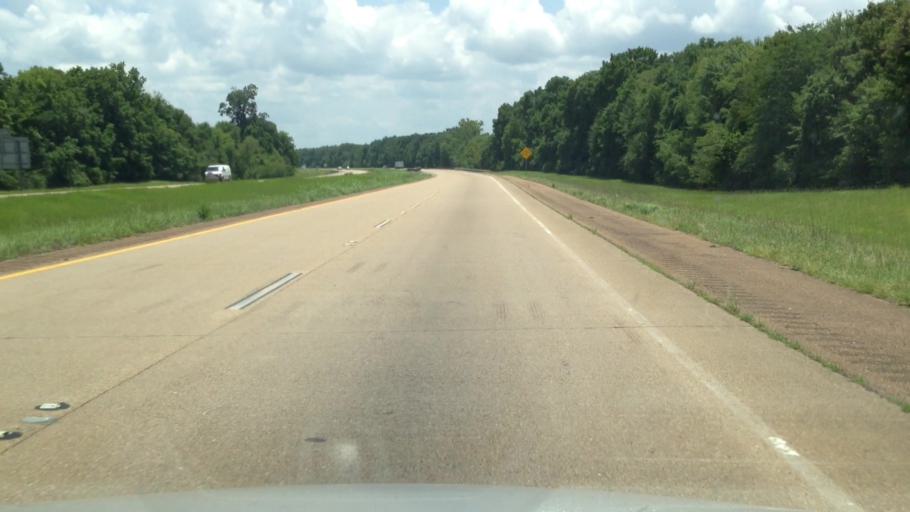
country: US
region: Louisiana
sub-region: Rapides Parish
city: Woodworth
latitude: 31.1462
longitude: -92.4529
